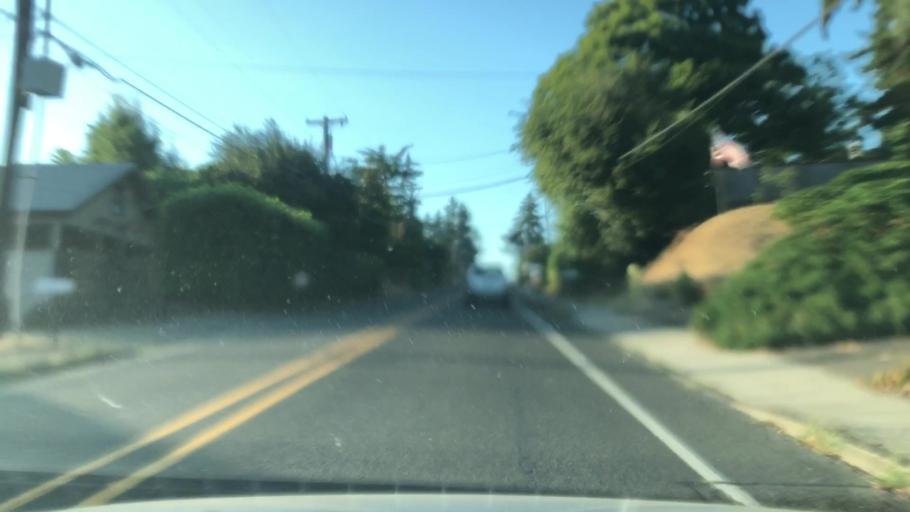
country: US
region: Oregon
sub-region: Clackamas County
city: Oak Grove
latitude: 45.4151
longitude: -122.6455
